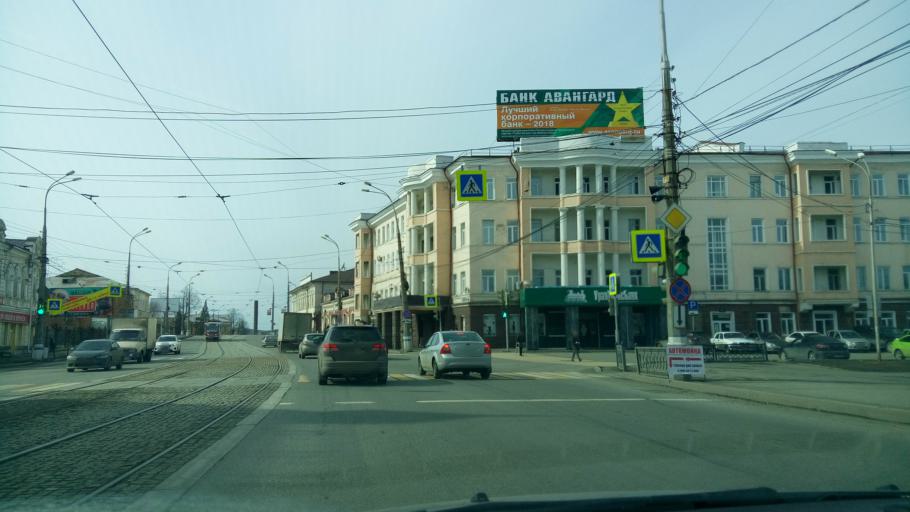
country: RU
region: Sverdlovsk
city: Nizhniy Tagil
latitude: 57.9072
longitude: 59.9559
